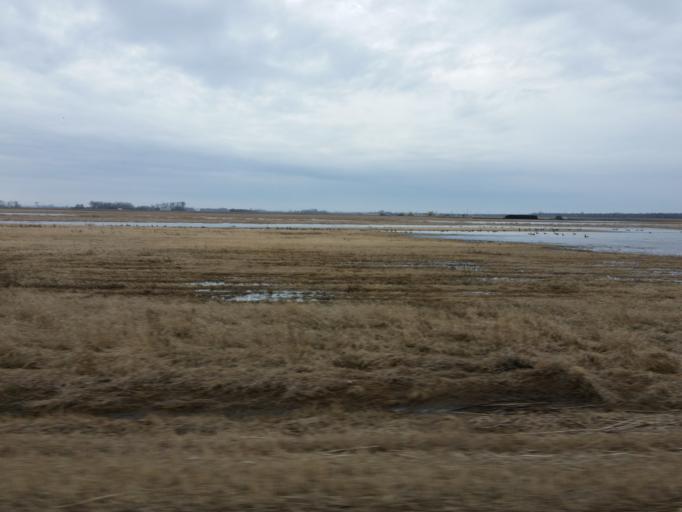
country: US
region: North Dakota
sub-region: Walsh County
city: Grafton
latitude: 48.4099
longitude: -97.4702
